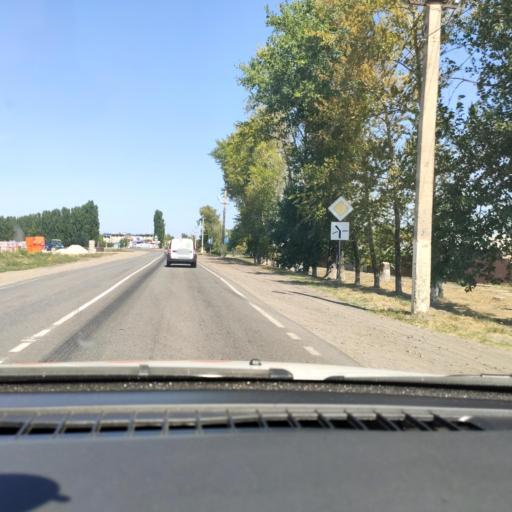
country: RU
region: Voronezj
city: Imeni Pervogo Maya
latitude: 50.7126
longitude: 39.4066
